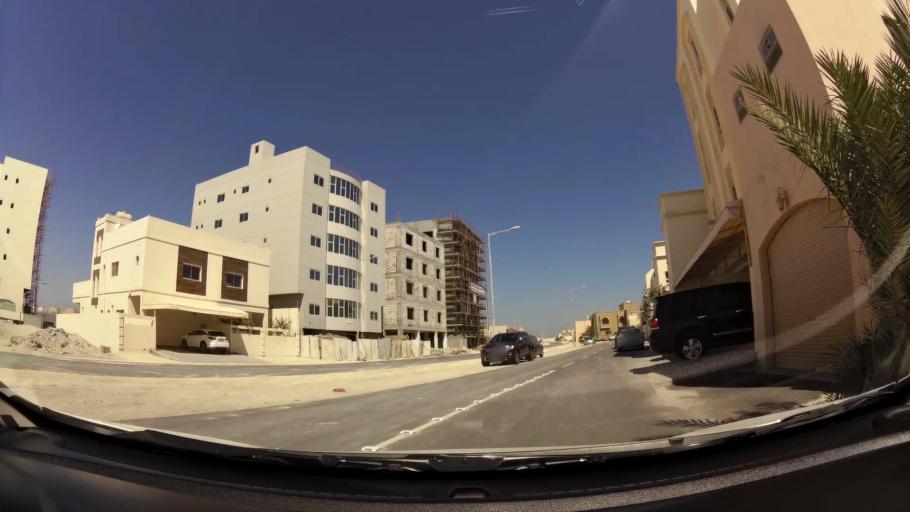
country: BH
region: Muharraq
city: Al Muharraq
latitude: 26.2730
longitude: 50.6005
